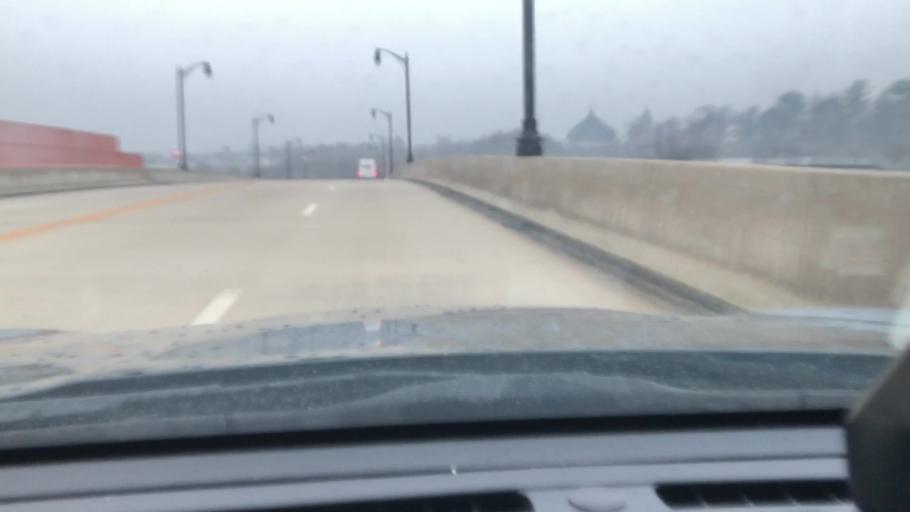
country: US
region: Pennsylvania
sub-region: Lehigh County
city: Fullerton
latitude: 40.6238
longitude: -75.4578
